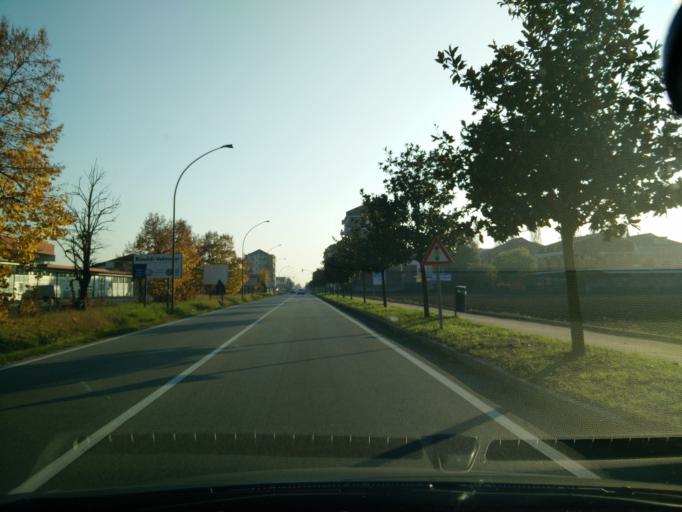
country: IT
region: Piedmont
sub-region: Provincia di Torino
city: Leini
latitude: 45.1708
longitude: 7.7130
